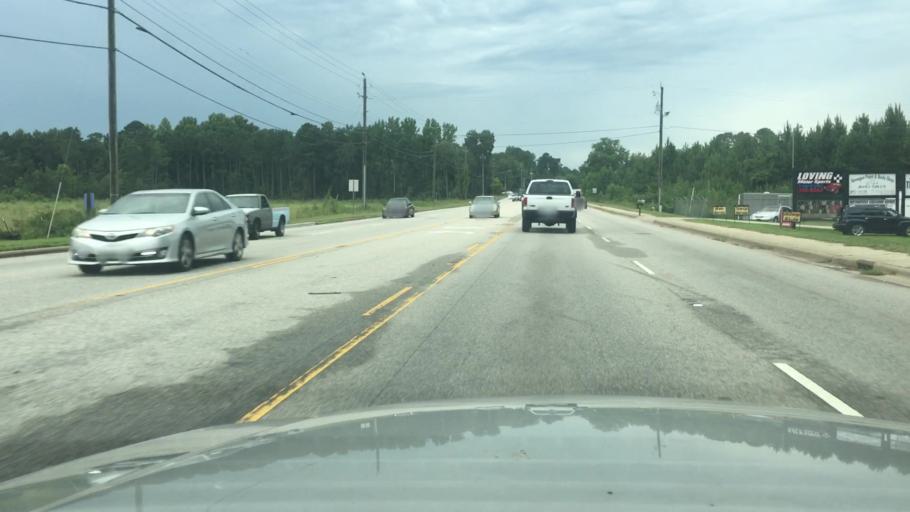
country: US
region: North Carolina
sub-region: Cumberland County
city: Hope Mills
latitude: 34.9901
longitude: -78.9666
